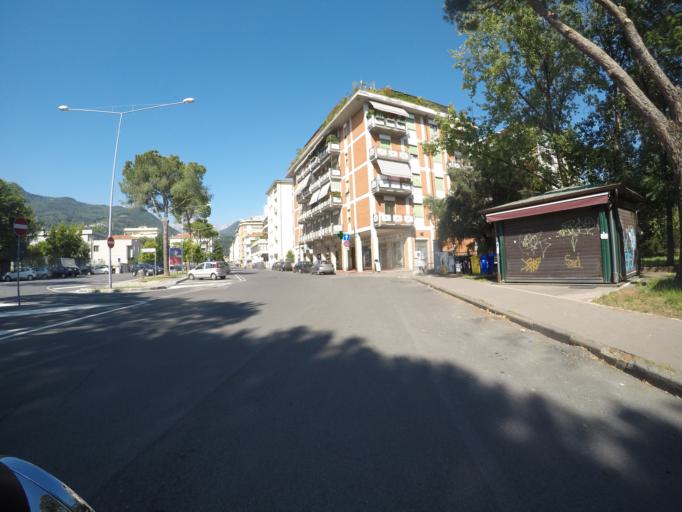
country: IT
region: Tuscany
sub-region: Provincia di Massa-Carrara
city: Massa
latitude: 44.0343
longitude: 10.1342
